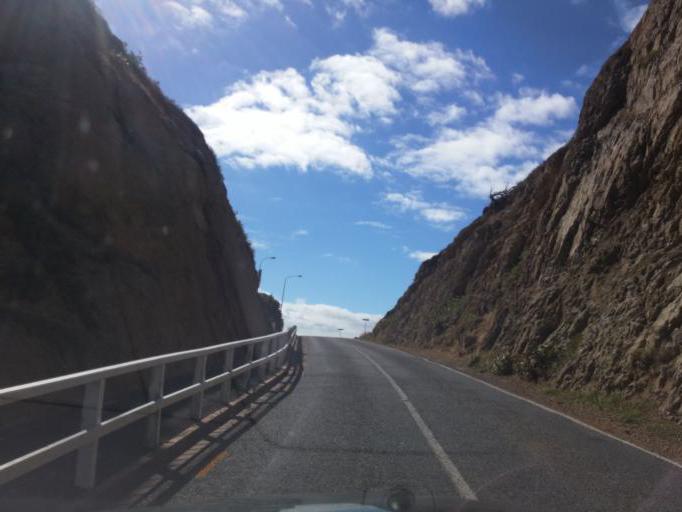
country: NZ
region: Wellington
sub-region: Wellington City
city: Wellington
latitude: -41.3293
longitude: 174.8324
